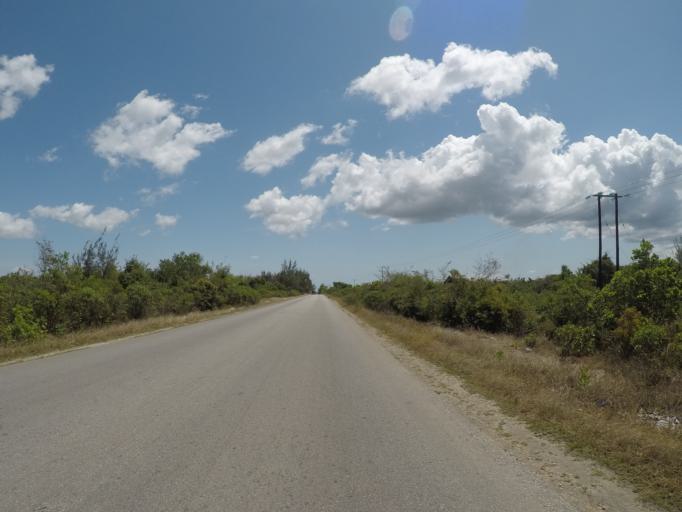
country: TZ
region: Zanzibar Central/South
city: Nganane
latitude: -6.2683
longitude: 39.5199
